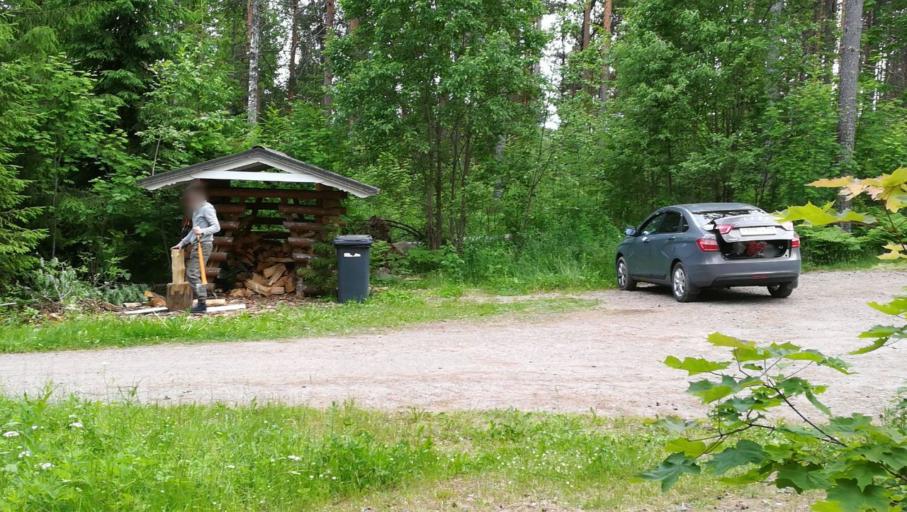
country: FI
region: South Karelia
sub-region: Imatra
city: Rautjaervi
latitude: 61.4840
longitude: 29.2290
